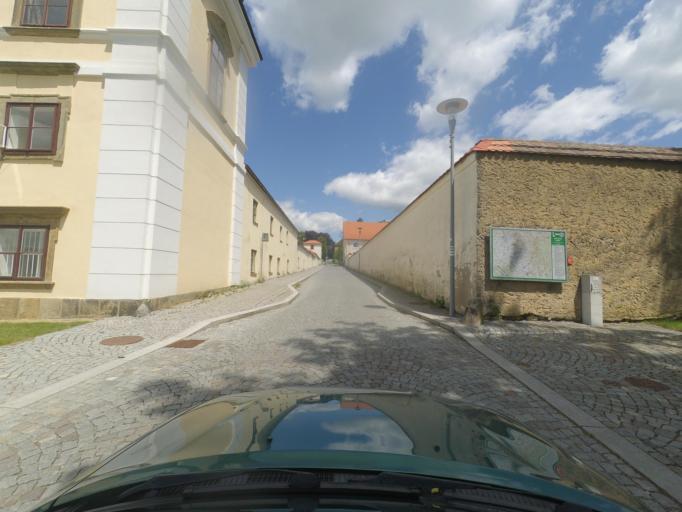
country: CZ
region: Kralovehradecky
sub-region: Okres Rychnov nad Kneznou
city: Rychnov nad Kneznou
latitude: 50.1658
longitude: 16.2758
